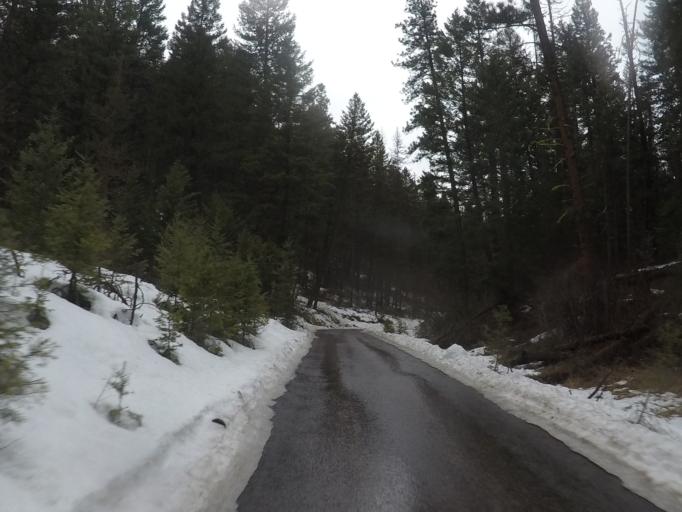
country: US
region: Montana
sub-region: Missoula County
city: East Missoula
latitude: 46.9255
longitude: -113.9644
